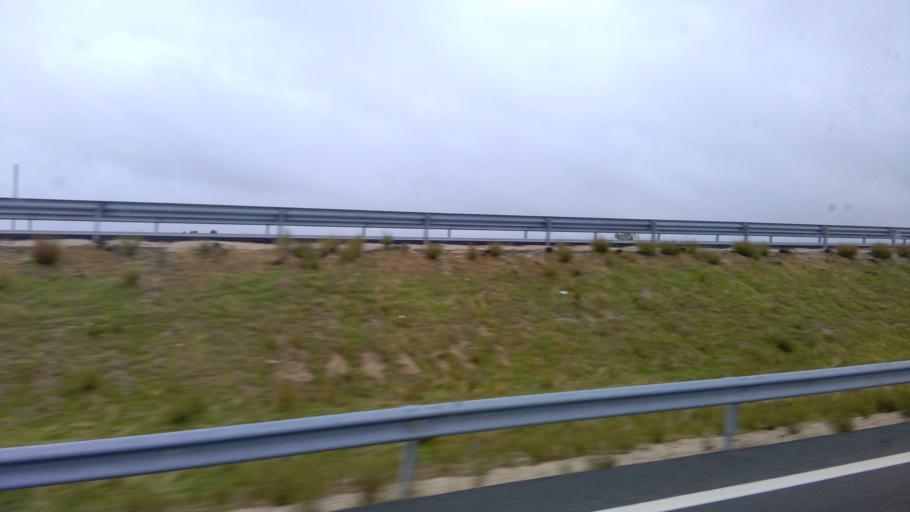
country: ES
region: Castille-La Mancha
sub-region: Province of Toledo
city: Las Ventas de Retamosa
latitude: 40.1739
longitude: -4.1543
